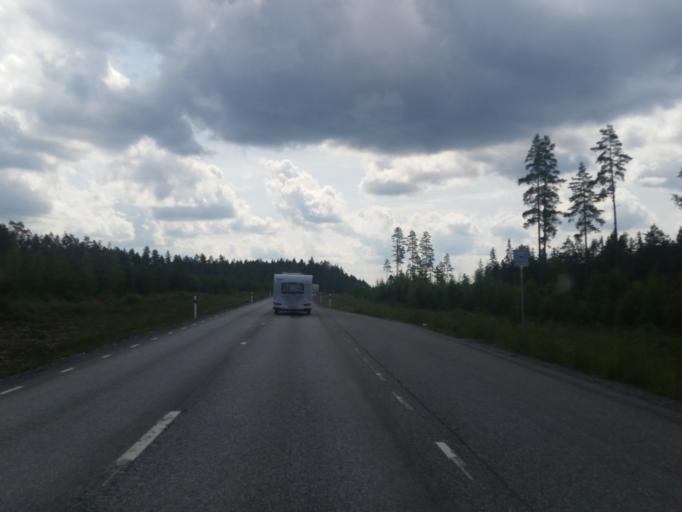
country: SE
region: OErebro
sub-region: Ljusnarsbergs Kommun
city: Kopparberg
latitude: 59.9653
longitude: 15.0204
